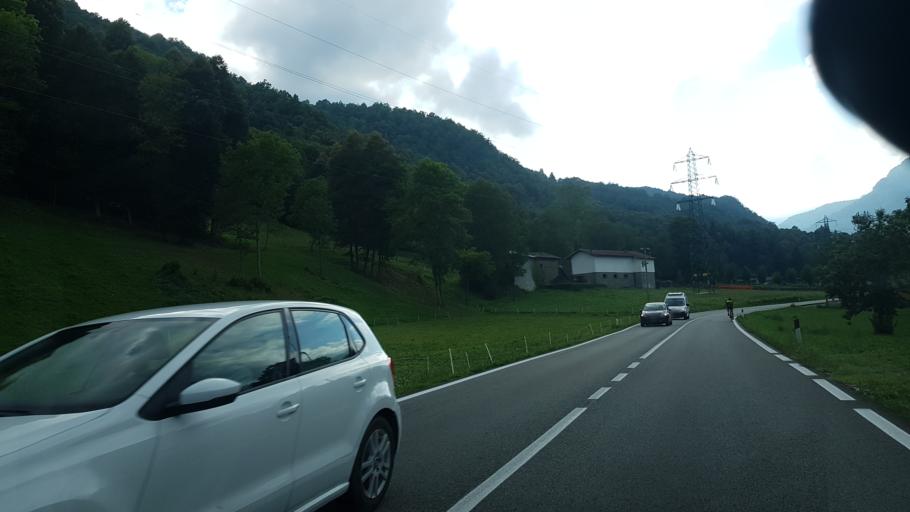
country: IT
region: Piedmont
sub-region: Provincia di Cuneo
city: Melle
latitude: 44.5616
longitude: 7.3100
